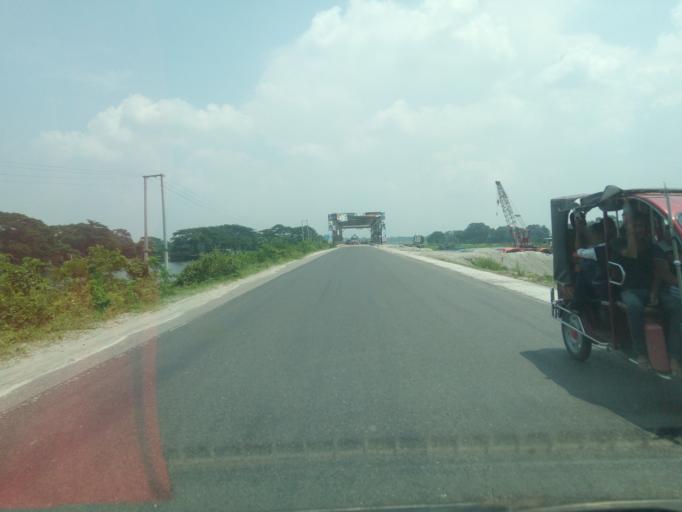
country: BD
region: Dhaka
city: Char Bhadrasan
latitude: 23.3816
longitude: 90.0037
